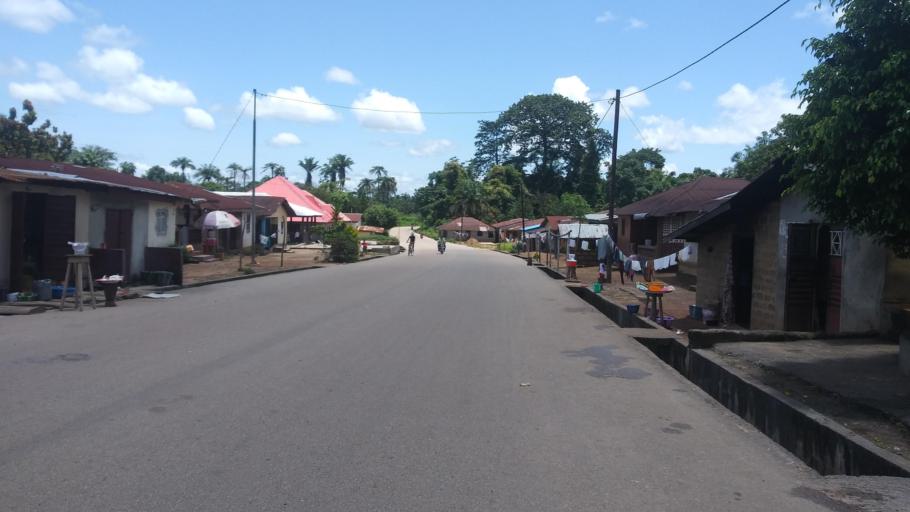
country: SL
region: Northern Province
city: Makeni
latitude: 8.8794
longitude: -12.0241
